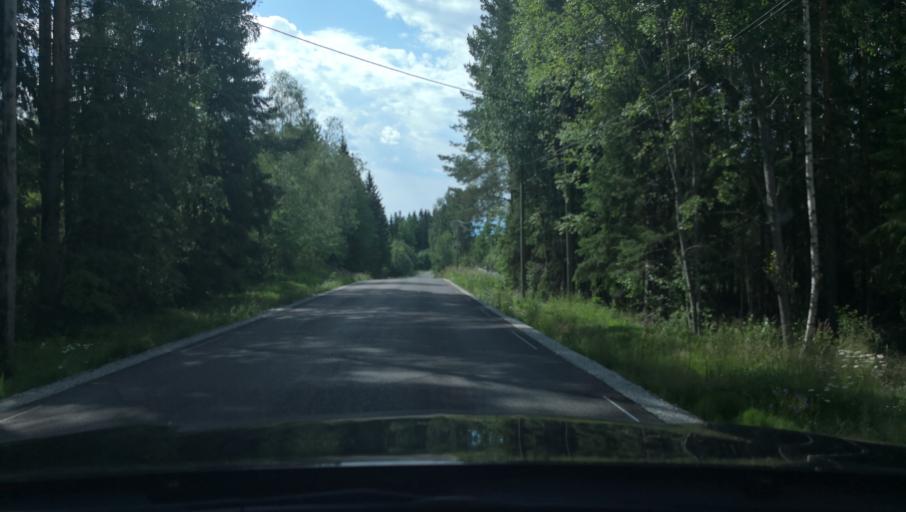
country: SE
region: Vaestmanland
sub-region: Norbergs Kommun
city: Norberg
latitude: 59.9669
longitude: 15.9824
